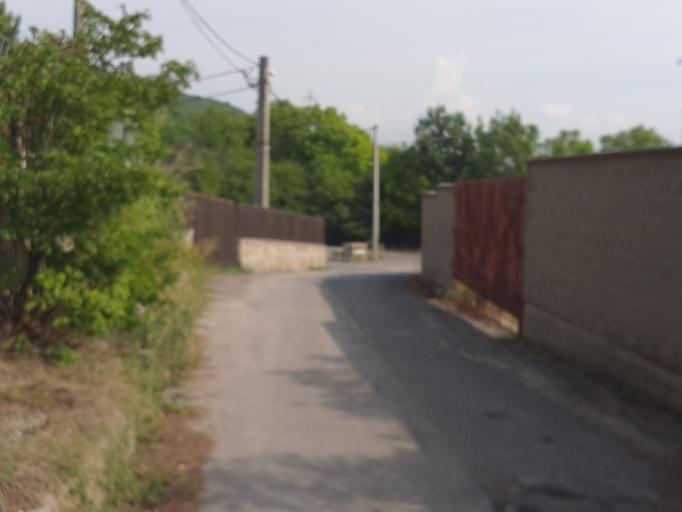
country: SK
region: Bratislavsky
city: Bratislava
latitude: 48.1751
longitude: 17.1166
